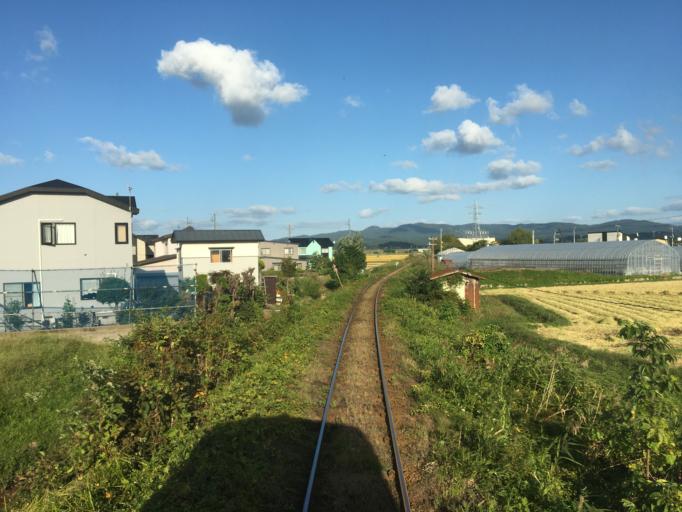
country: JP
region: Aomori
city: Goshogawara
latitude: 40.8177
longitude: 140.4576
